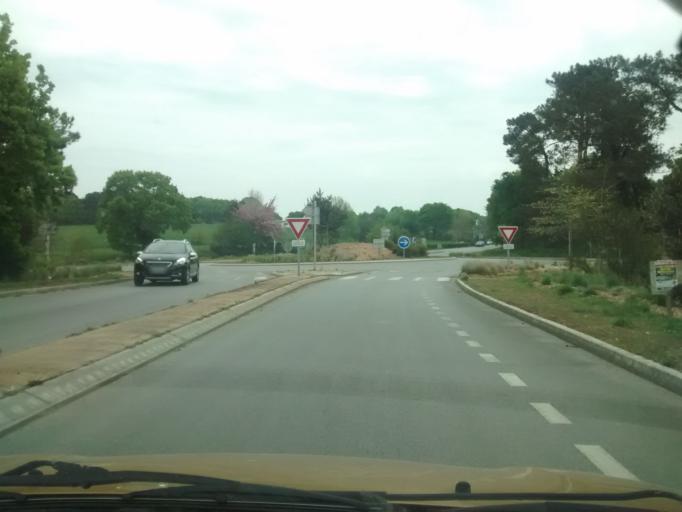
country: FR
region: Brittany
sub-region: Departement du Morbihan
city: Berric
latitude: 47.6146
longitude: -2.5402
